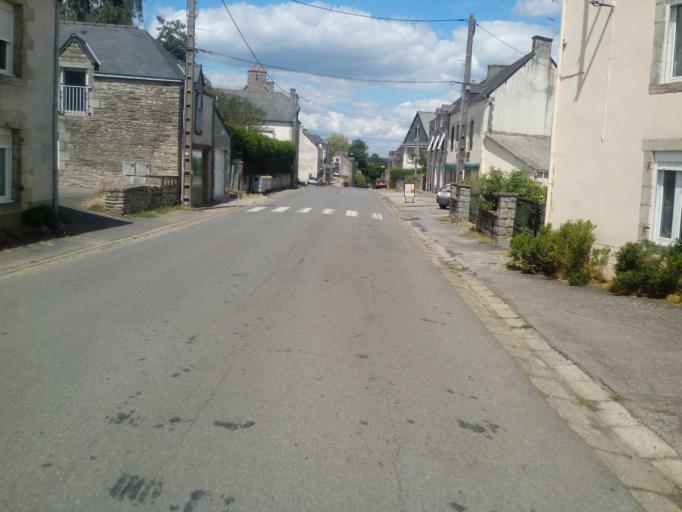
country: FR
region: Brittany
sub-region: Departement du Morbihan
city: Guegon
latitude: 47.9370
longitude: -2.5649
